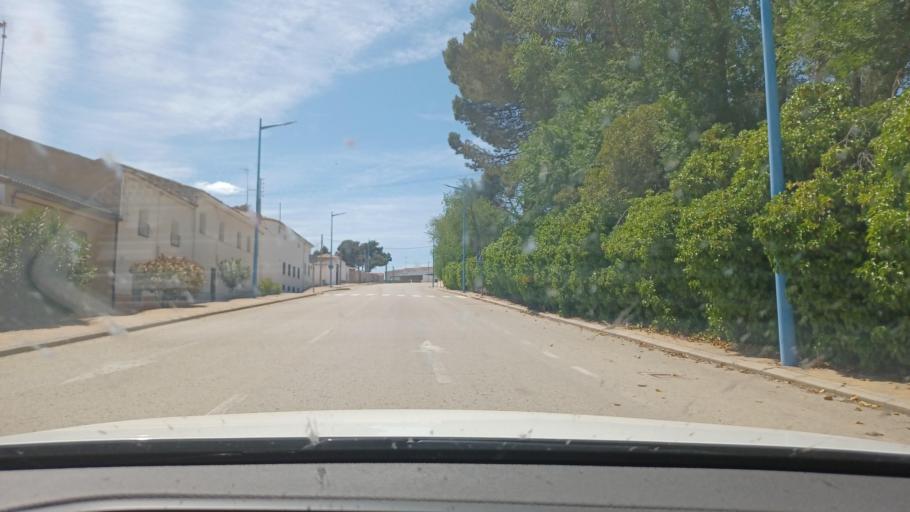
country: ES
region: Castille-La Mancha
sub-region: Provincia de Cuenca
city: Montalbo
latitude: 39.8814
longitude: -2.6713
